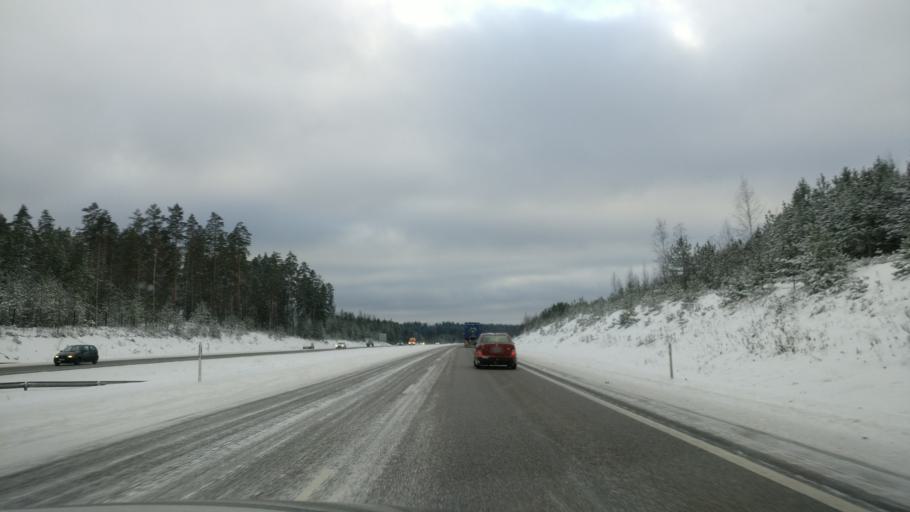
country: FI
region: Paijanne Tavastia
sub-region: Lahti
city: Nastola
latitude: 61.1056
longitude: 25.9146
